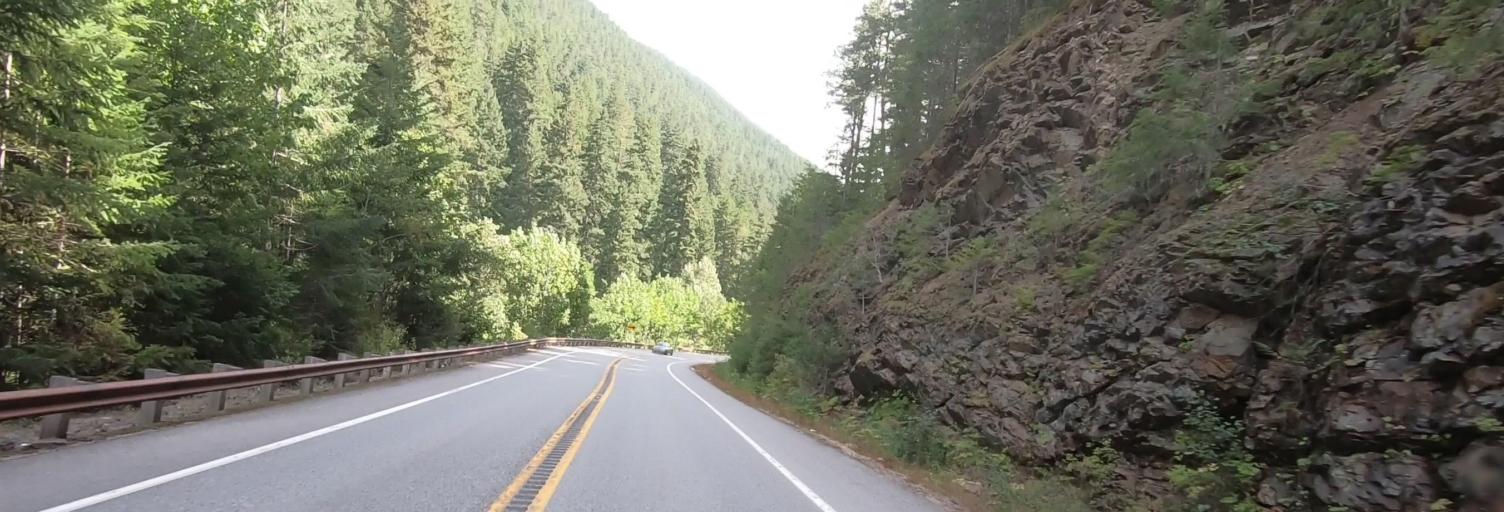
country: US
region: Washington
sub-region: Snohomish County
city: Darrington
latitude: 48.6937
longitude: -120.9115
